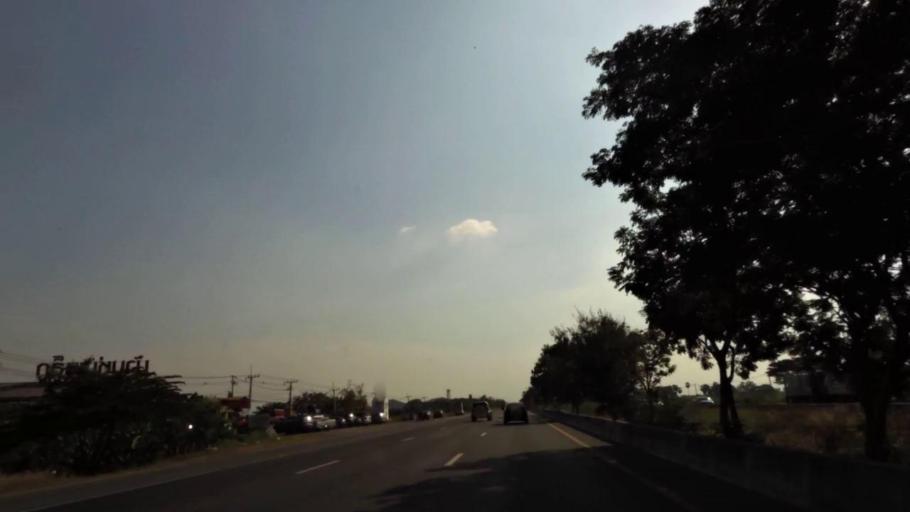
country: TH
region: Ang Thong
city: Ban Thai Tan
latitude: 14.6277
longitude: 100.4724
